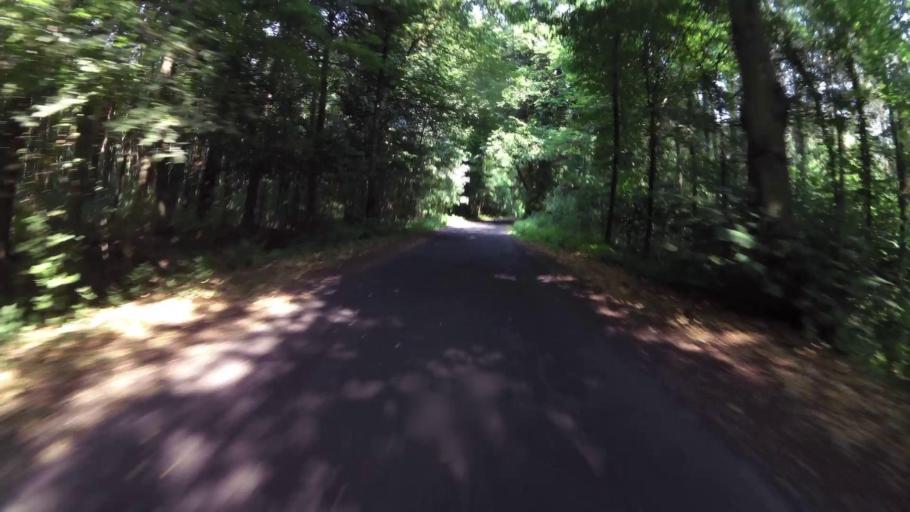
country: PL
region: West Pomeranian Voivodeship
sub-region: Powiat gryfinski
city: Mieszkowice
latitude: 52.8508
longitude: 14.5168
